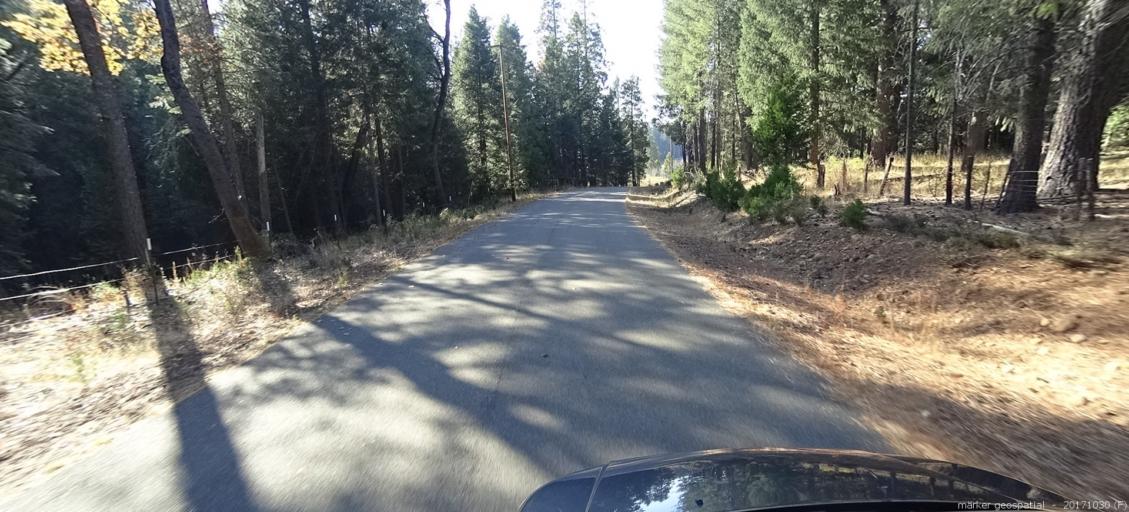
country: US
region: California
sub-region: Shasta County
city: Shingletown
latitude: 40.5339
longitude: -121.7210
